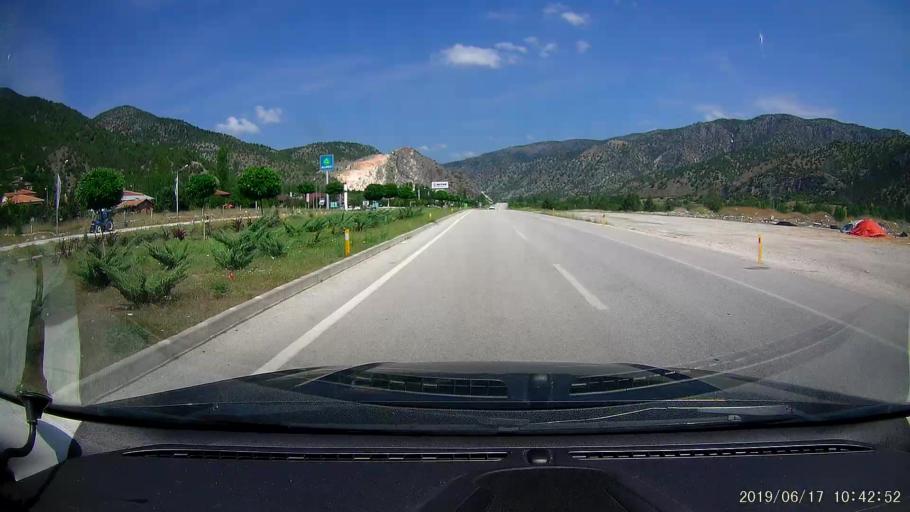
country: TR
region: Corum
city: Kargi
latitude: 41.0541
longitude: 34.5455
